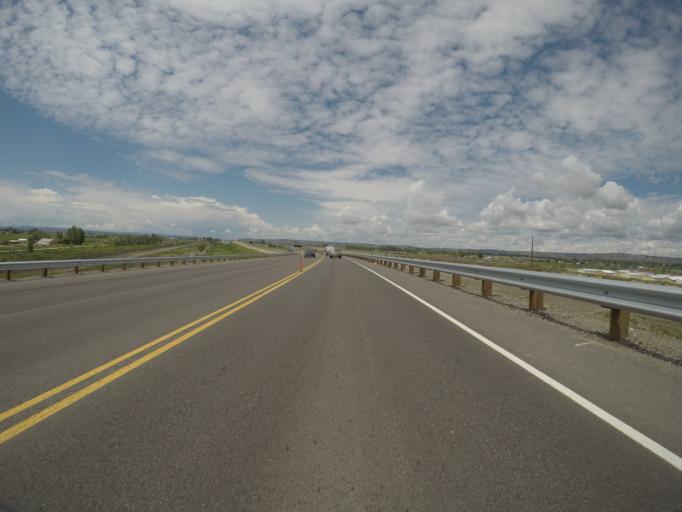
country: US
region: Montana
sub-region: Yellowstone County
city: Laurel
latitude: 45.6640
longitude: -108.7925
